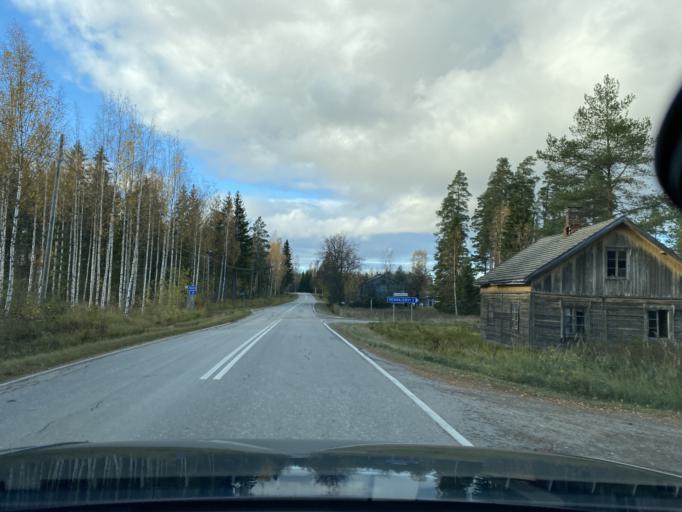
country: FI
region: Pirkanmaa
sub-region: Lounais-Pirkanmaa
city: Punkalaidun
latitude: 61.0337
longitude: 23.2315
